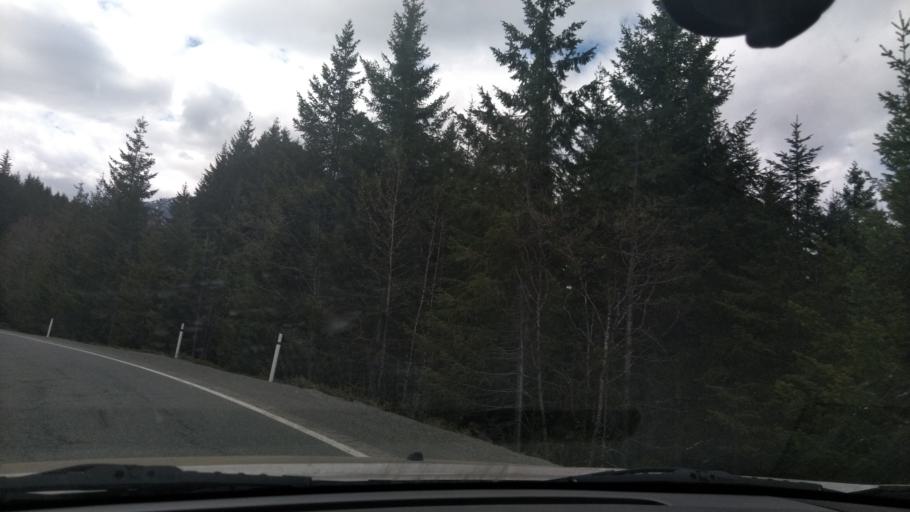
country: CA
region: British Columbia
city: Campbell River
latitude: 49.8690
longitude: -125.6490
